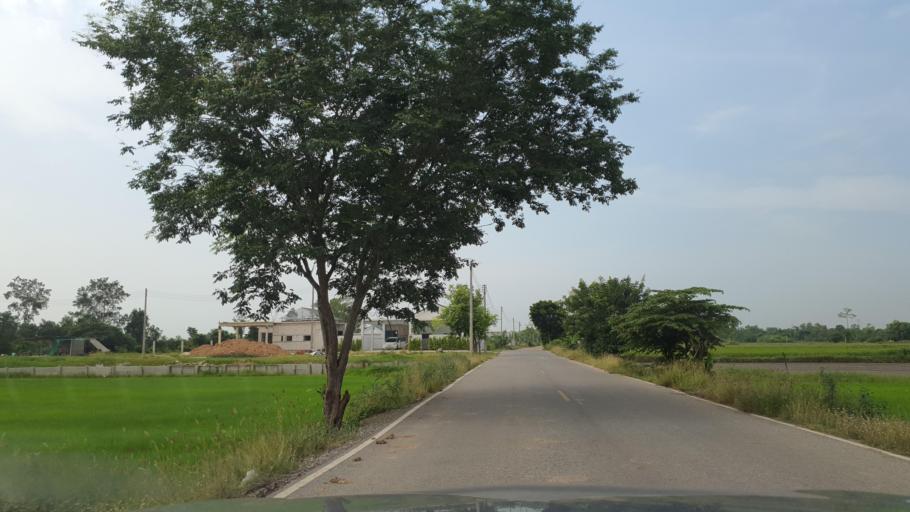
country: TH
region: Phitsanulok
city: Bang Rakam
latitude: 16.8047
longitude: 100.1627
